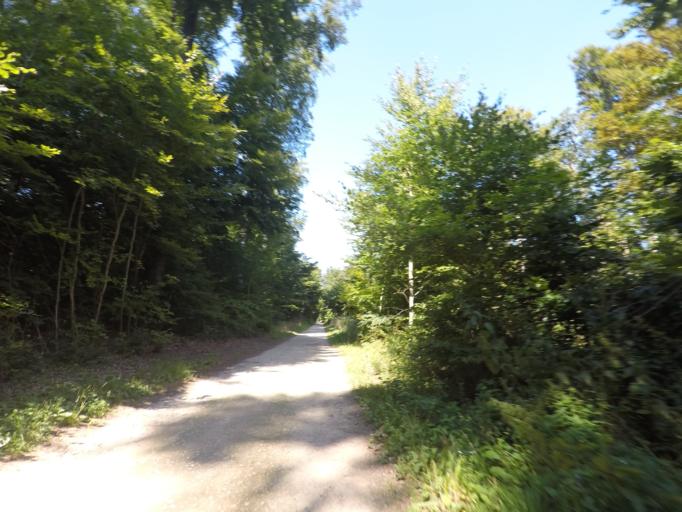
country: LU
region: Luxembourg
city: Bereldange
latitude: 49.6406
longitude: 6.1099
